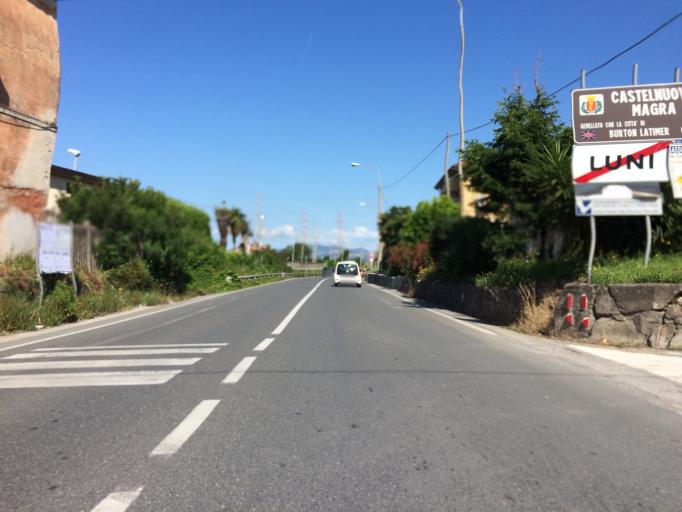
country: IT
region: Liguria
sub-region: Provincia di La Spezia
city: Colombiera-Molicciara
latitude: 44.0749
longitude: 10.0162
